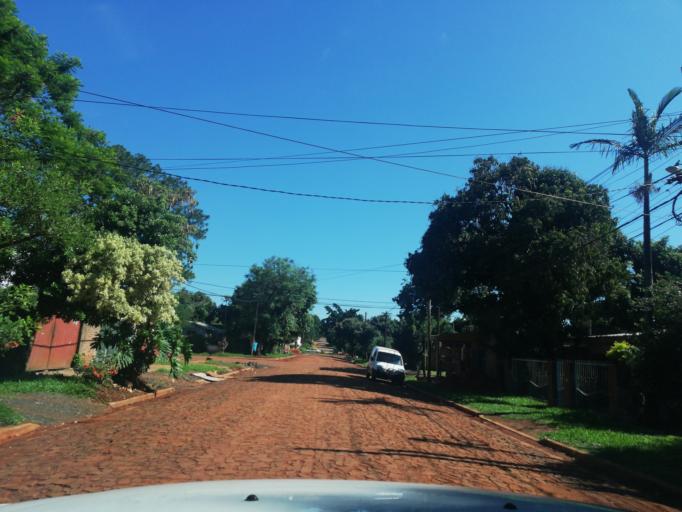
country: AR
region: Misiones
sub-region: Departamento de Capital
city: Posadas
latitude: -27.3975
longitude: -55.9226
